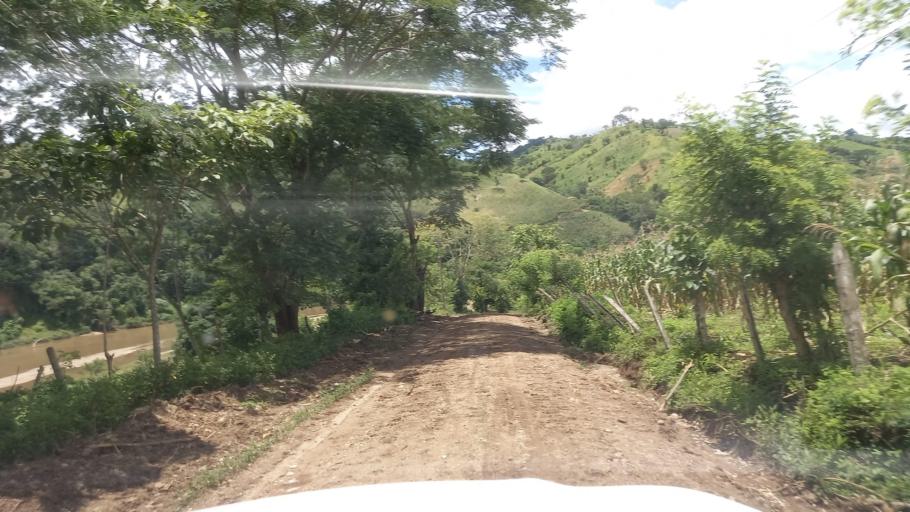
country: NI
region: Nueva Segovia
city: Wiwili
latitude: 13.7415
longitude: -85.7895
